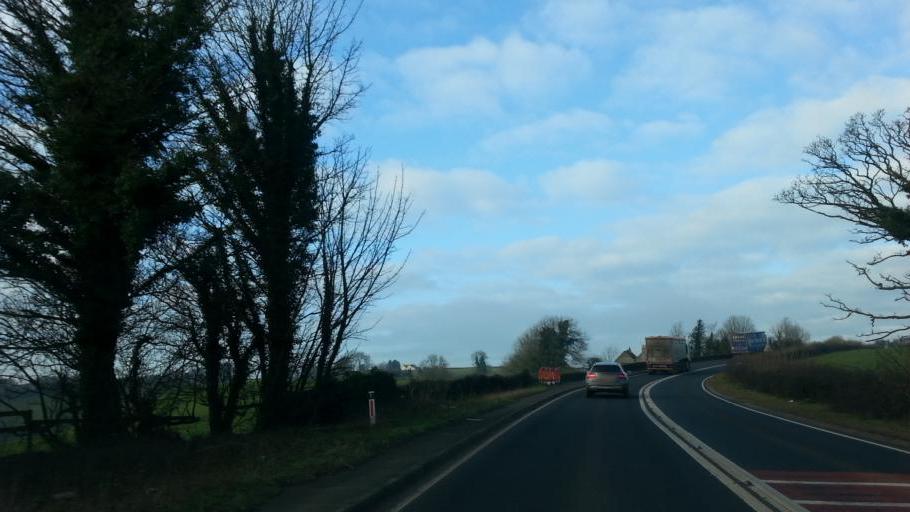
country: GB
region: England
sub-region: South Gloucestershire
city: Cold Ashton
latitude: 51.4456
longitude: -2.3651
